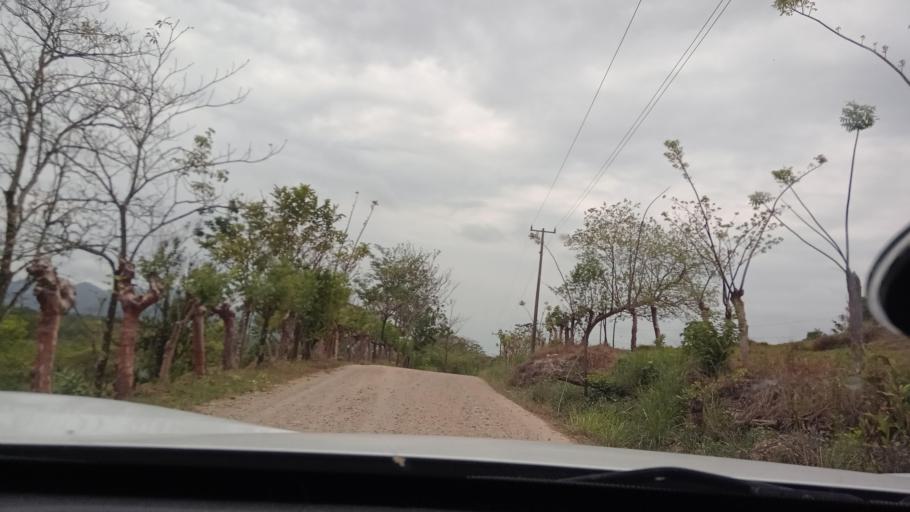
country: MX
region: Tabasco
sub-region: Huimanguillo
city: Francisco Rueda
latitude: 17.5807
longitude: -94.0829
